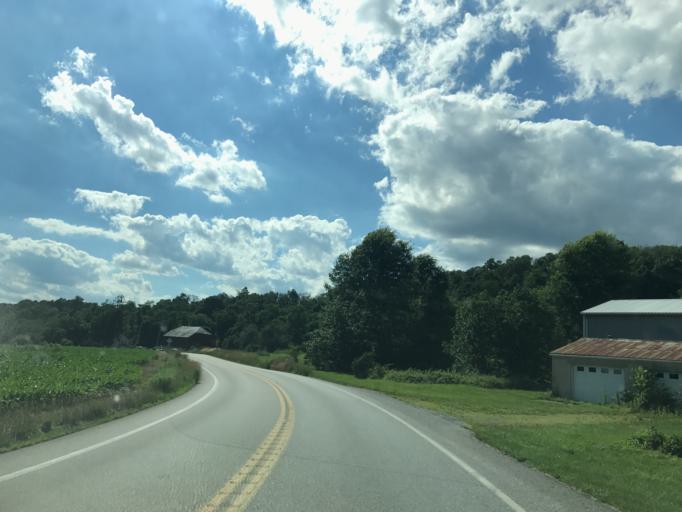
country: US
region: Pennsylvania
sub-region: York County
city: Glen Rock
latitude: 39.7396
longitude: -76.7813
